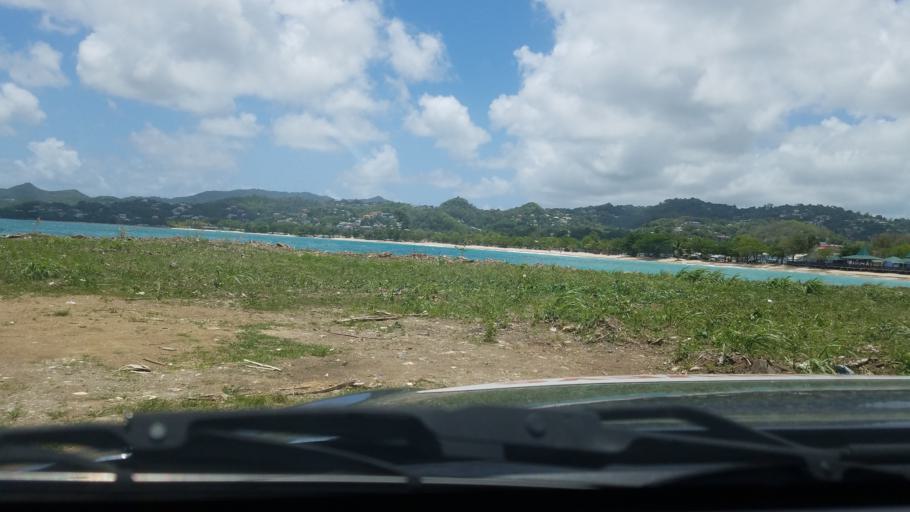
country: LC
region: Castries Quarter
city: Bisee
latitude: 14.0223
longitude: -60.9968
